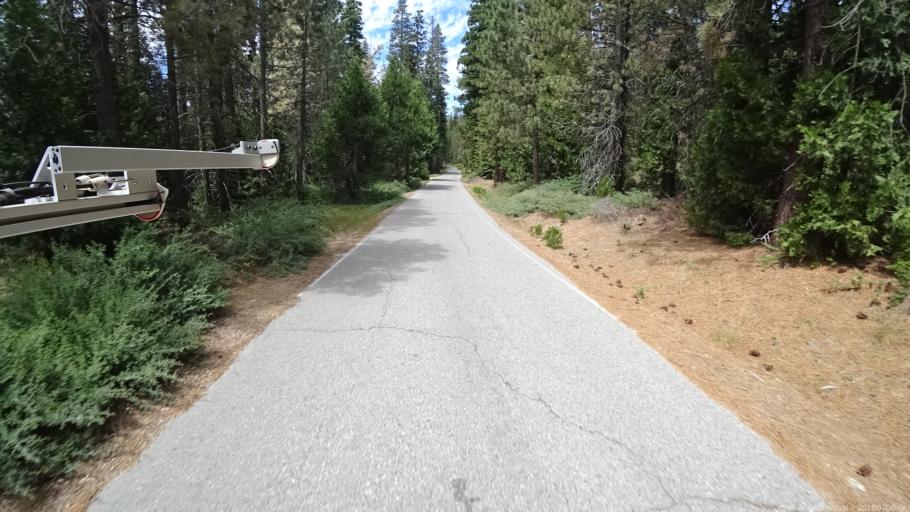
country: US
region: California
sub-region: Madera County
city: Oakhurst
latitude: 37.4277
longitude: -119.4190
